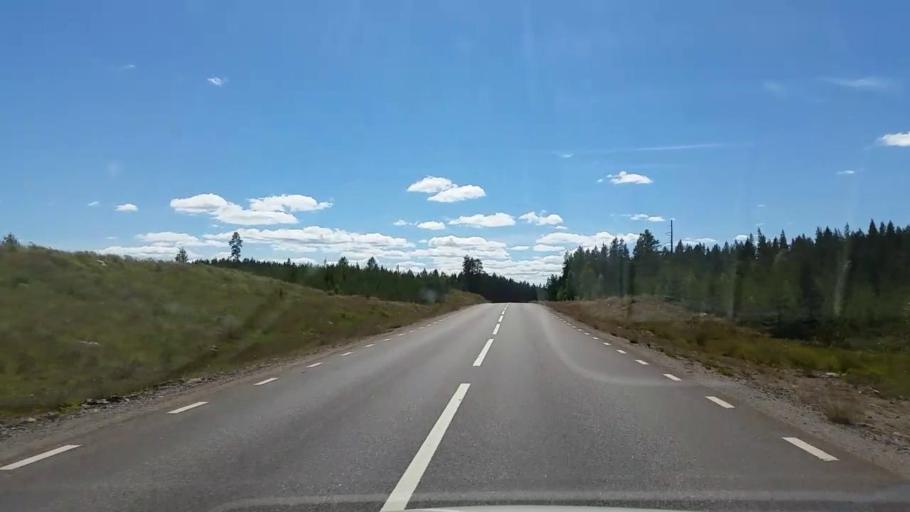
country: SE
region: Gaevleborg
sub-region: Bollnas Kommun
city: Vittsjo
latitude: 61.0947
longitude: 15.8262
